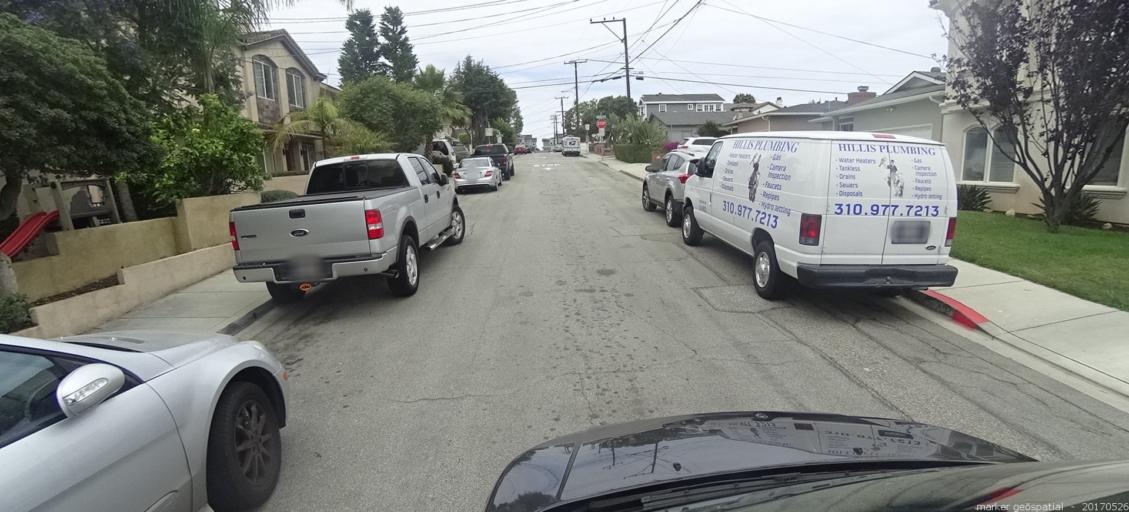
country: US
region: California
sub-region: Los Angeles County
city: Lawndale
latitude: 33.8809
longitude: -118.3764
